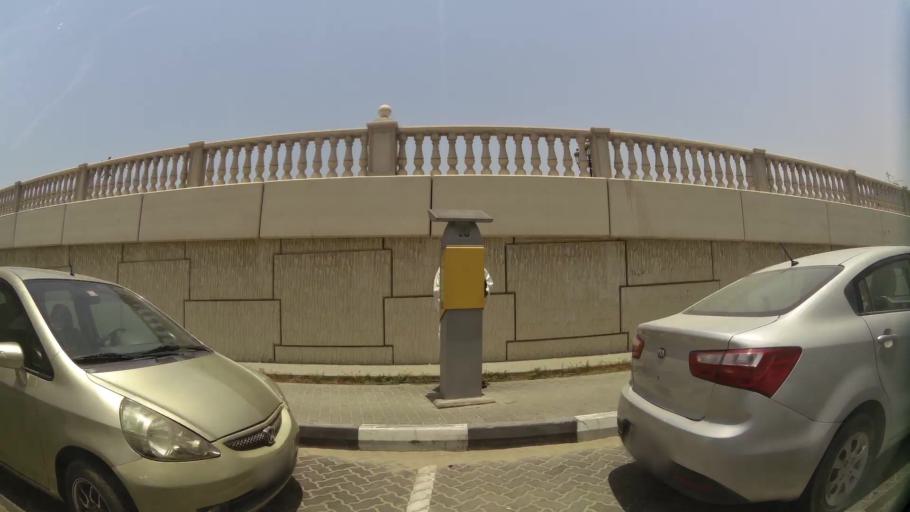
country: AE
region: Ash Shariqah
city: Sharjah
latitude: 25.3245
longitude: 55.3817
